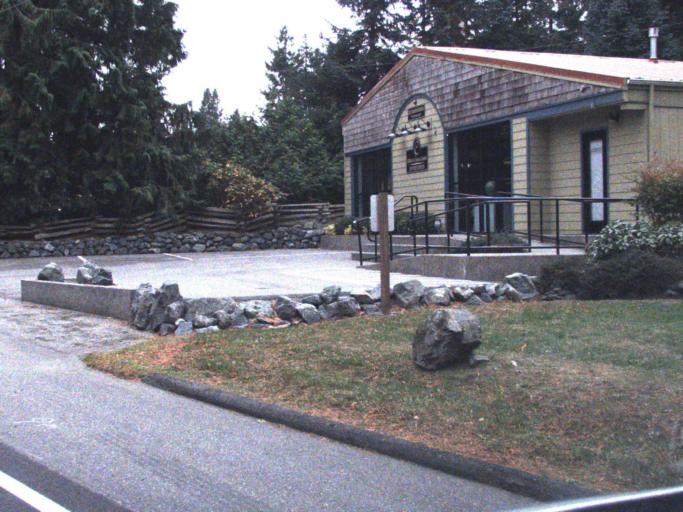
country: US
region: Washington
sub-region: Island County
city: Camano
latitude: 48.1005
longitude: -122.5742
